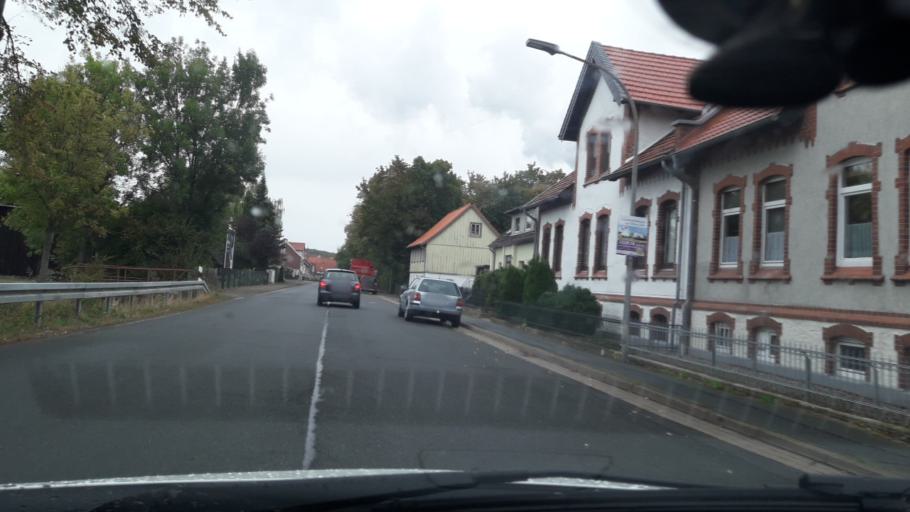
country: DE
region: Lower Saxony
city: Schladen
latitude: 52.0178
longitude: 10.5408
